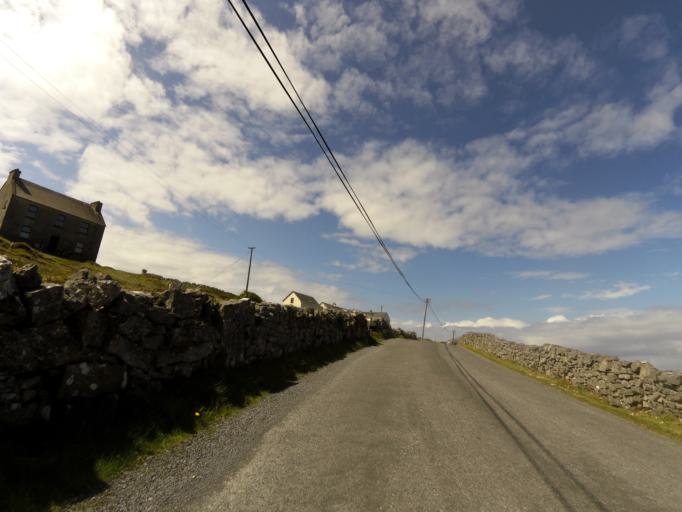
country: IE
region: Connaught
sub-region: County Galway
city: Oughterard
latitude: 53.1300
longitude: -9.6971
